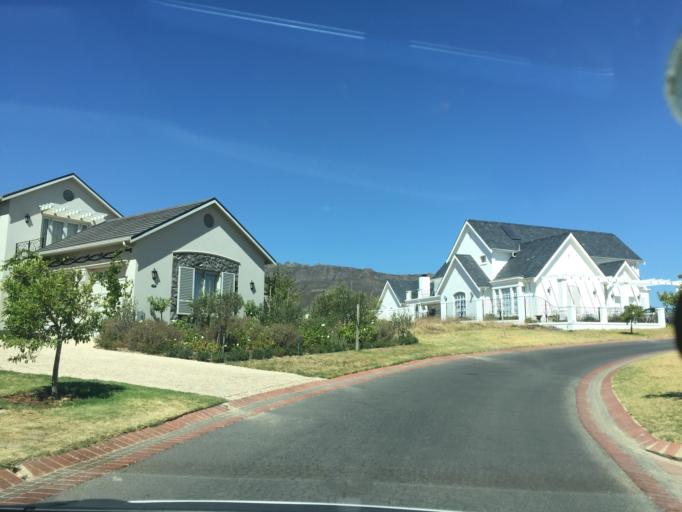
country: ZA
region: Western Cape
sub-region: Cape Winelands District Municipality
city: Paarl
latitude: -33.8058
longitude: 18.9783
